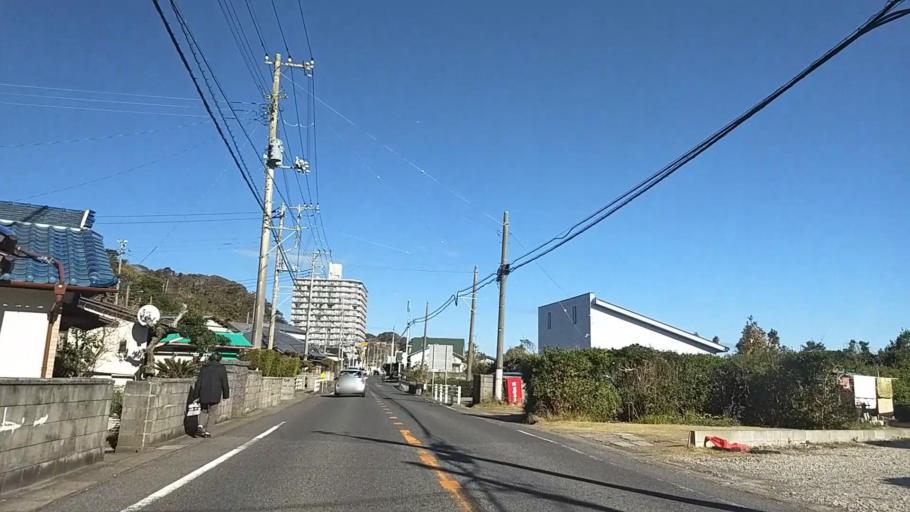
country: JP
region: Chiba
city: Katsuura
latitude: 35.1659
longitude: 140.3333
